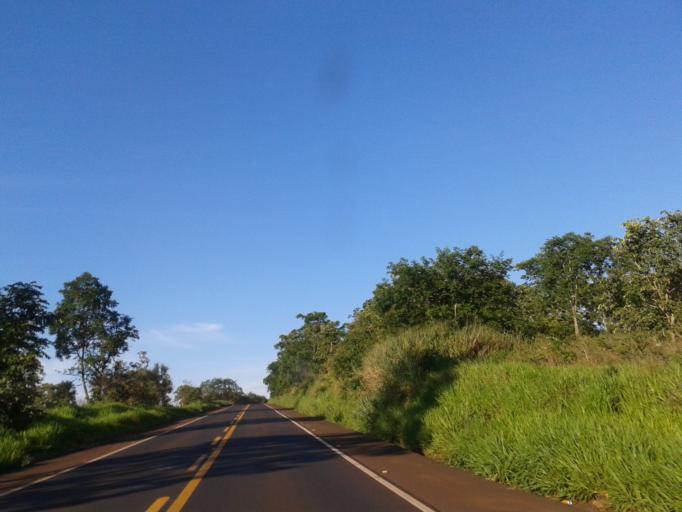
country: BR
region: Minas Gerais
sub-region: Santa Vitoria
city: Santa Vitoria
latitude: -18.9382
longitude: -49.8065
